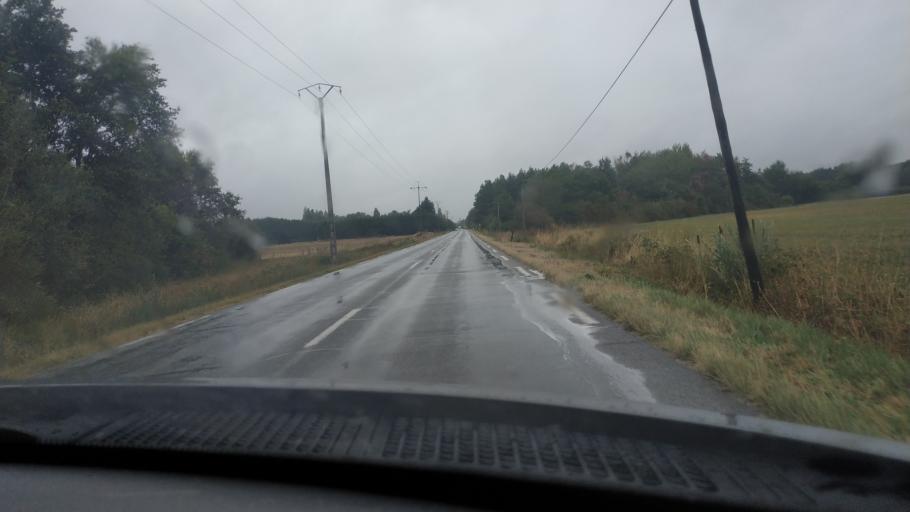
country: FR
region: Centre
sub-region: Departement du Loiret
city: Bellegarde
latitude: 47.9326
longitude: 2.3907
